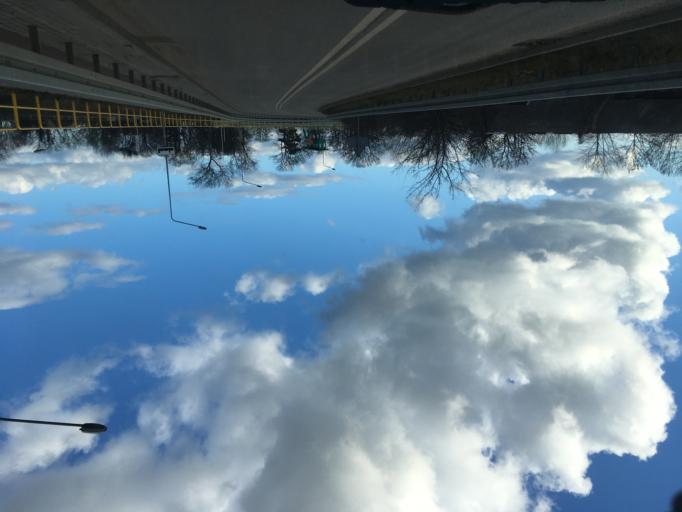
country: PL
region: Pomeranian Voivodeship
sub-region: Powiat nowodworski
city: Ostaszewo
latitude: 54.3075
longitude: 18.9249
